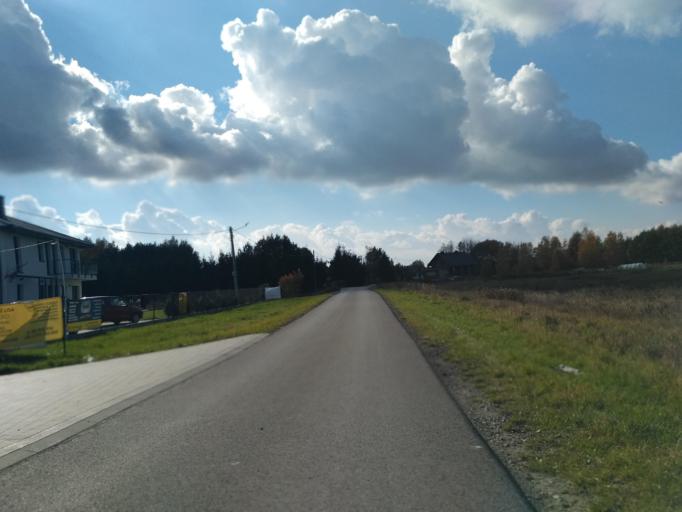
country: PL
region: Subcarpathian Voivodeship
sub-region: Powiat rzeszowski
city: Swilcza
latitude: 50.1223
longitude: 21.9052
